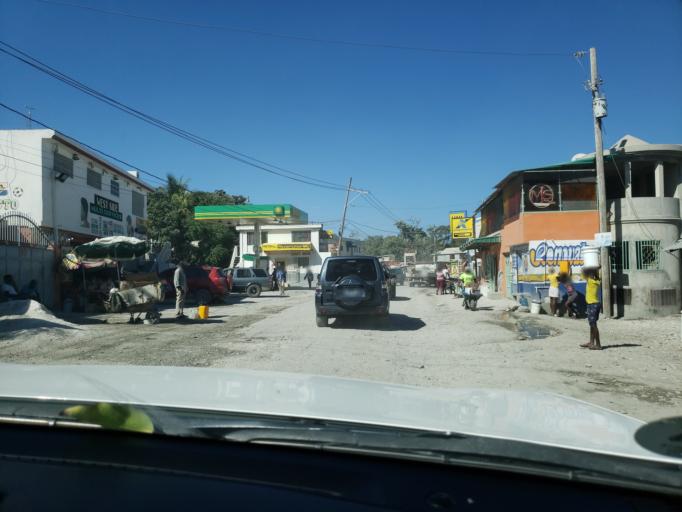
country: HT
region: Ouest
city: Croix des Bouquets
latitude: 18.5734
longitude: -72.2269
